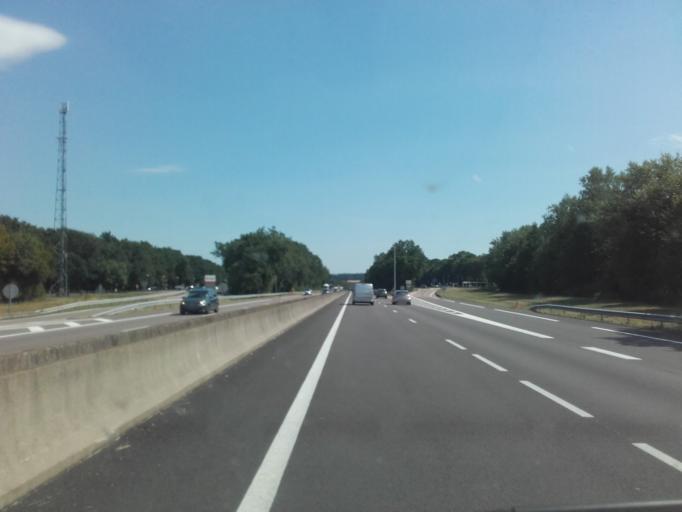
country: FR
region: Bourgogne
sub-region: Departement de la Cote-d'Or
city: Semur-en-Auxois
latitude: 47.3917
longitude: 4.3628
